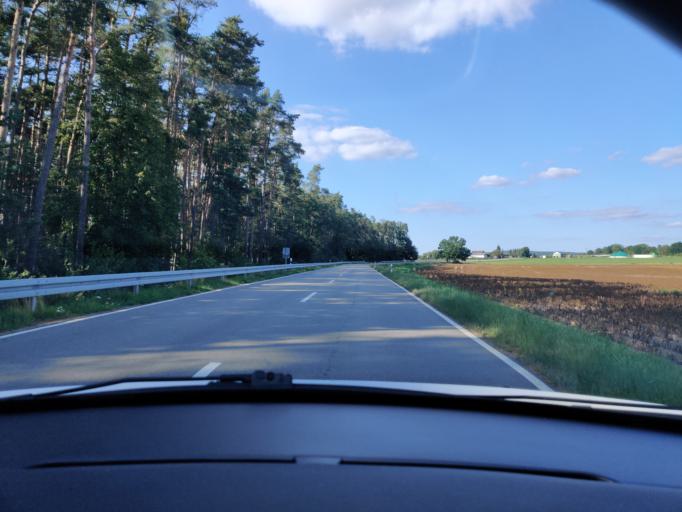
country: DE
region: Bavaria
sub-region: Upper Palatinate
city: Schwarzenfeld
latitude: 49.3552
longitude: 12.1467
